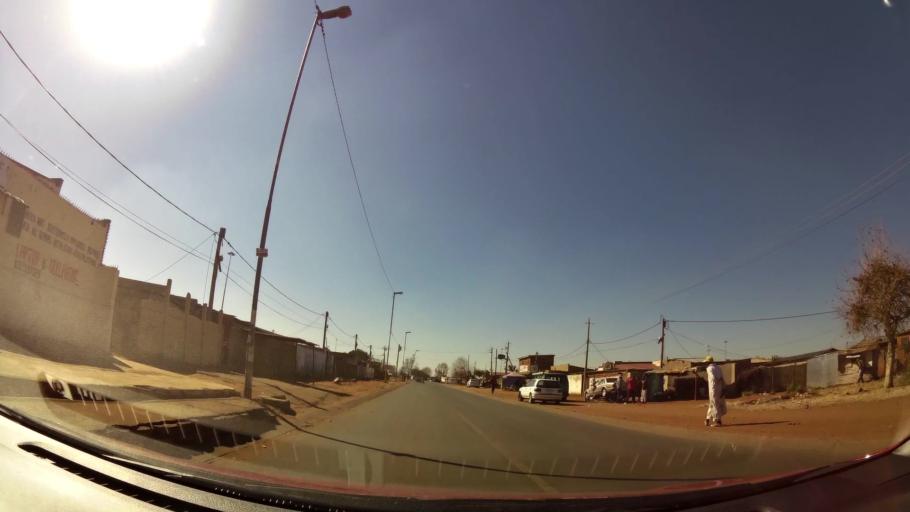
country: ZA
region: Gauteng
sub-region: City of Johannesburg Metropolitan Municipality
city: Soweto
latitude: -26.2237
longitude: 27.8317
